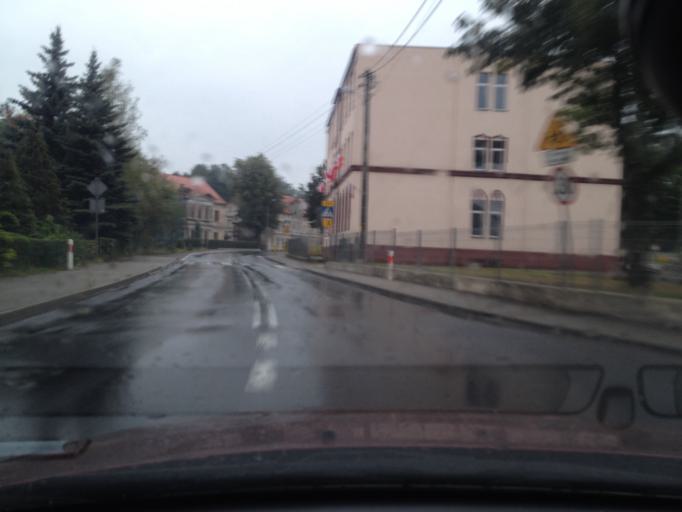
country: PL
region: Lubusz
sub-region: Powiat zaganski
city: Gozdnica
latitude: 51.3991
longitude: 15.1809
